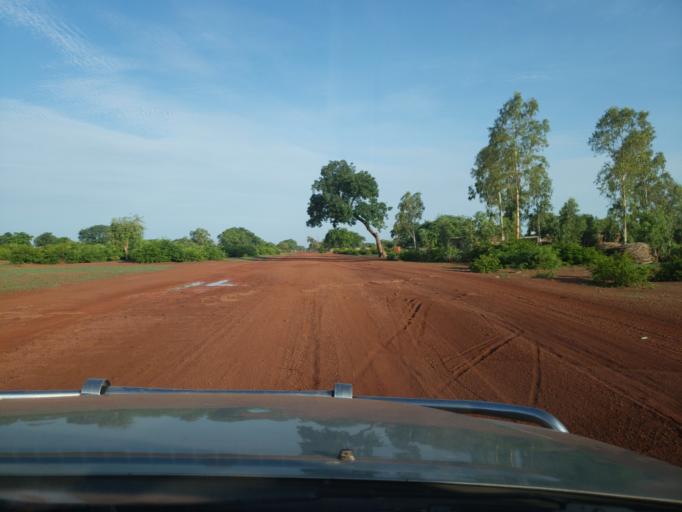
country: ML
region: Sikasso
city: Koutiala
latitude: 12.4174
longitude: -5.5738
